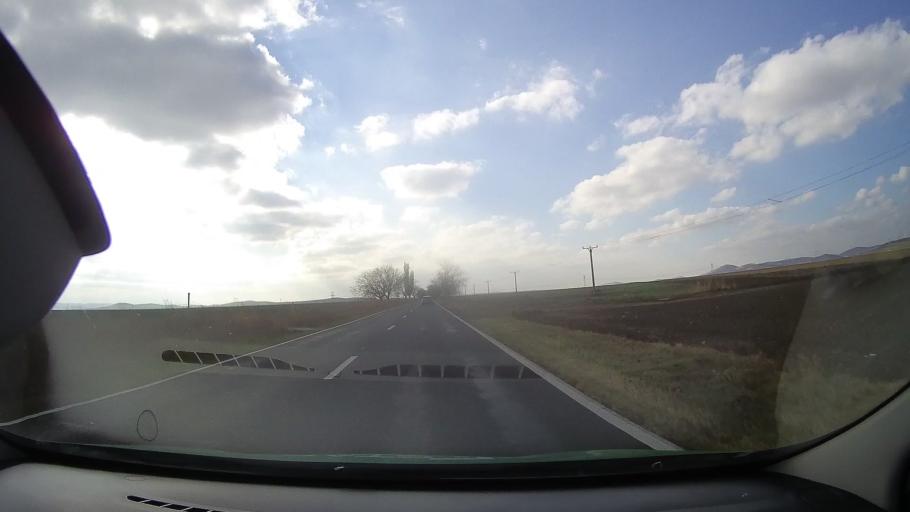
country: RO
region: Tulcea
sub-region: Comuna Nalbant
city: Nalbant
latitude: 45.0630
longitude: 28.6376
